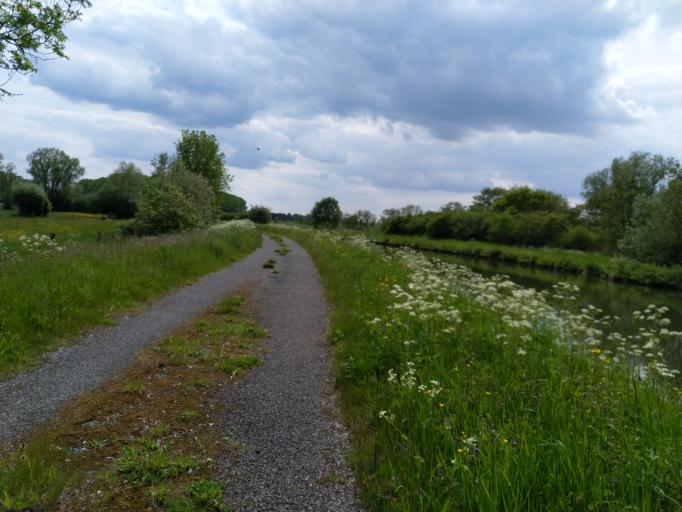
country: FR
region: Picardie
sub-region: Departement de l'Aisne
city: Wassigny
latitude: 50.0582
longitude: 3.6434
